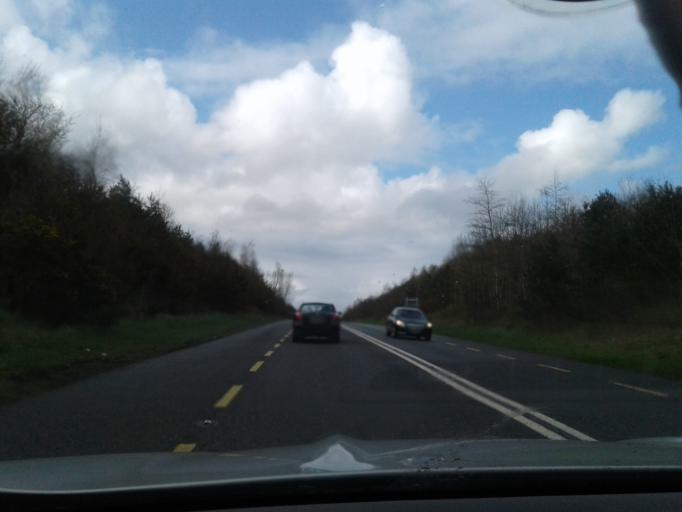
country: IE
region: Ulster
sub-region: County Monaghan
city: Carrickmacross
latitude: 53.9743
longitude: -6.7014
